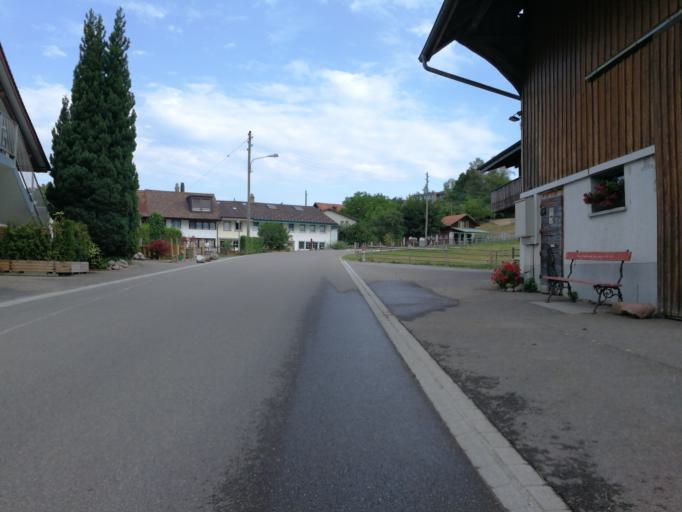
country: CH
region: Zurich
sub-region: Bezirk Hinwil
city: Gossau
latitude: 47.3292
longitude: 8.7602
